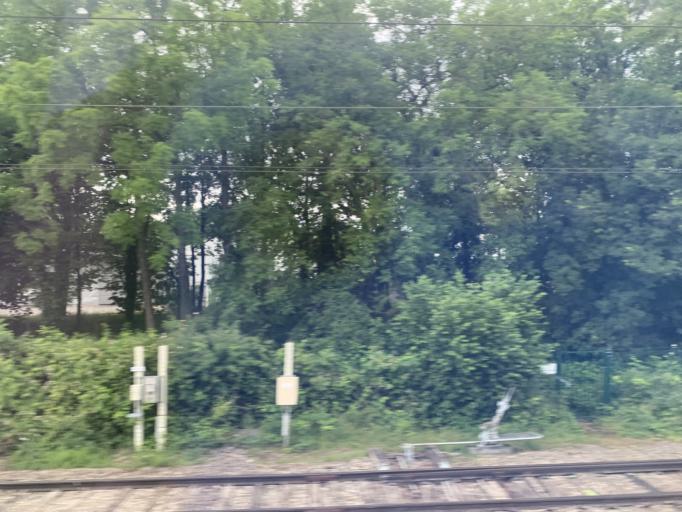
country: FR
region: Alsace
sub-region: Departement du Haut-Rhin
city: Aspach
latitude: 47.6282
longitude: 7.2317
